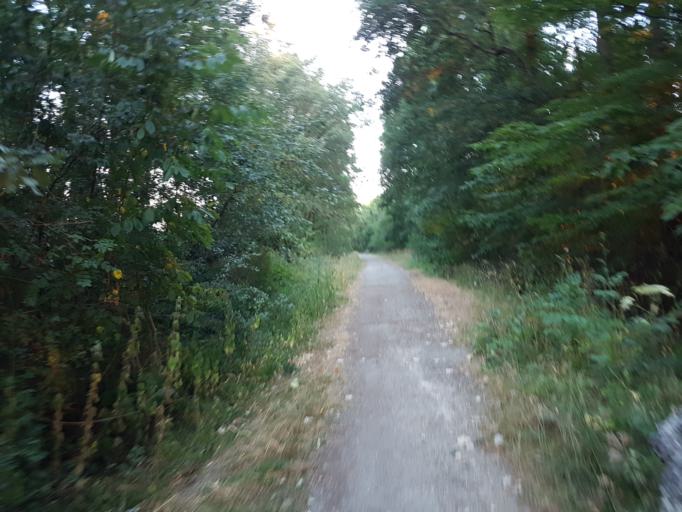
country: FR
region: Centre
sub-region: Departement d'Indre-et-Loire
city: Saint-Avertin
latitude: 47.3508
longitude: 0.7606
